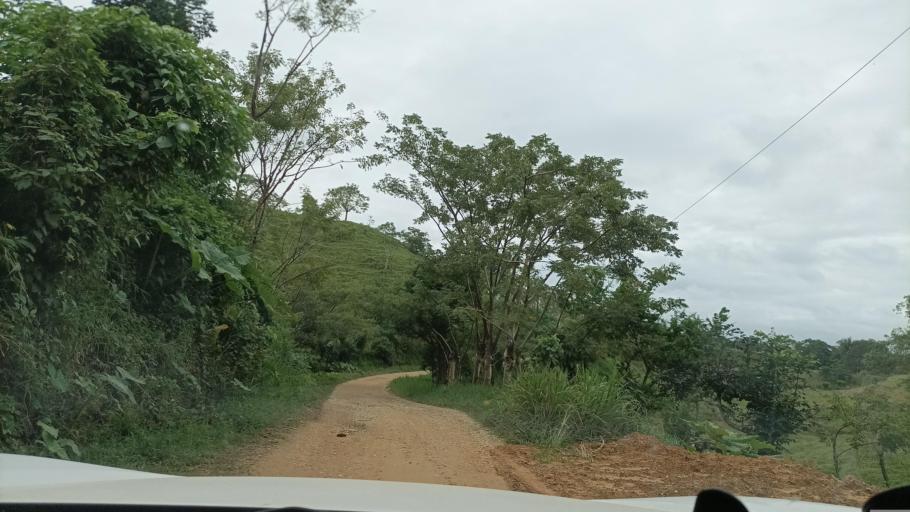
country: MX
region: Veracruz
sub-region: Uxpanapa
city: Poblado 10
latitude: 17.5636
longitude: -94.4244
